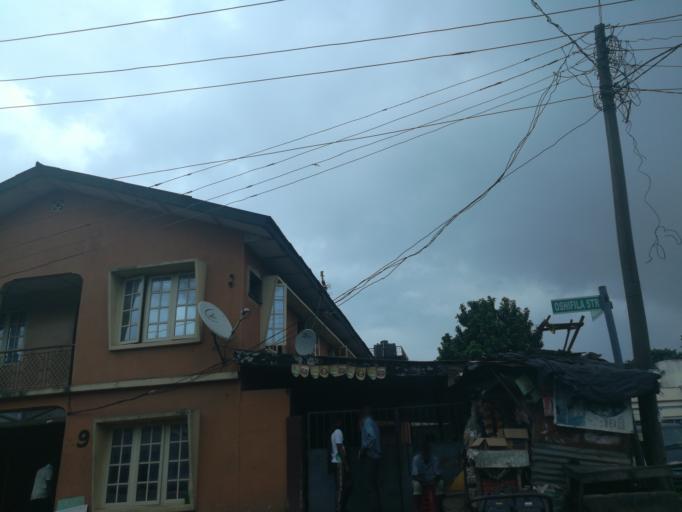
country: NG
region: Lagos
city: Ikeja
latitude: 6.6005
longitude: 3.3364
